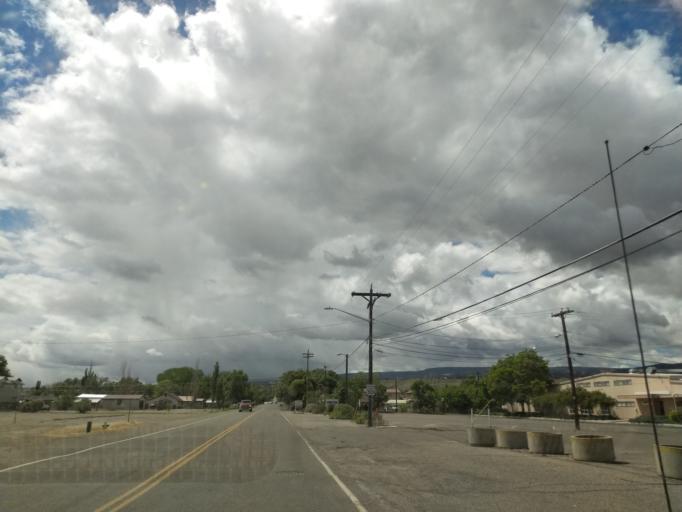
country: US
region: Colorado
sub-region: Mesa County
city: Orchard Mesa
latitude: 39.0477
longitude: -108.5524
